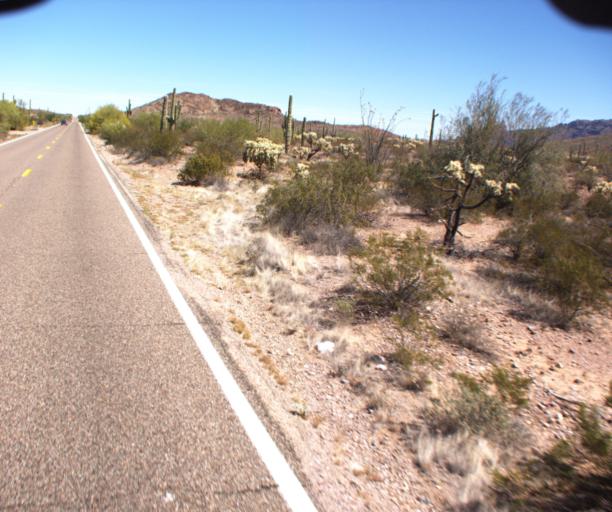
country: MX
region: Sonora
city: Sonoyta
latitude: 32.0730
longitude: -112.7821
